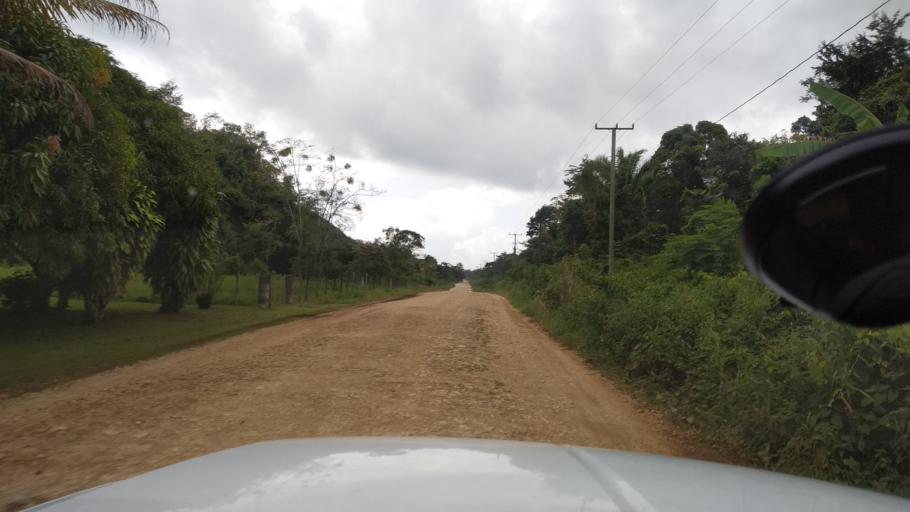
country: BZ
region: Toledo
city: Punta Gorda
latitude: 16.2121
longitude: -89.0192
